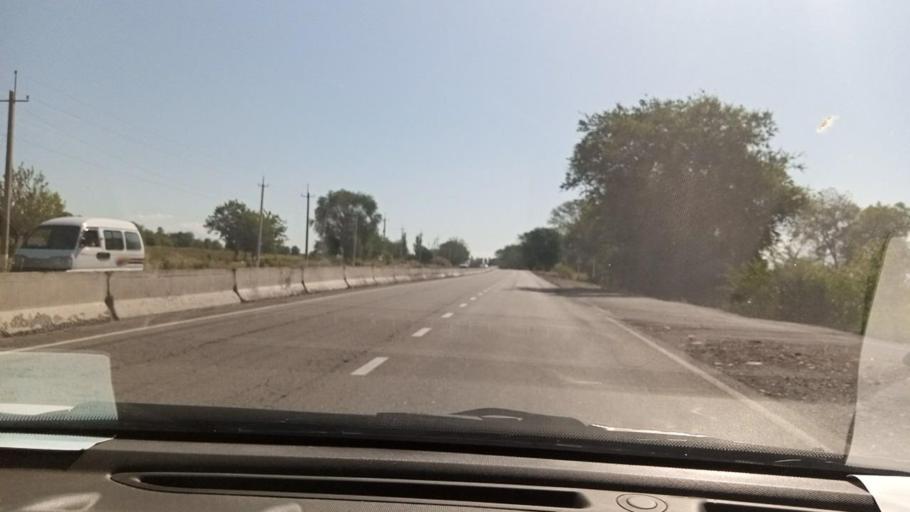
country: UZ
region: Toshkent
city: Ohangaron
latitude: 40.9334
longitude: 69.8834
